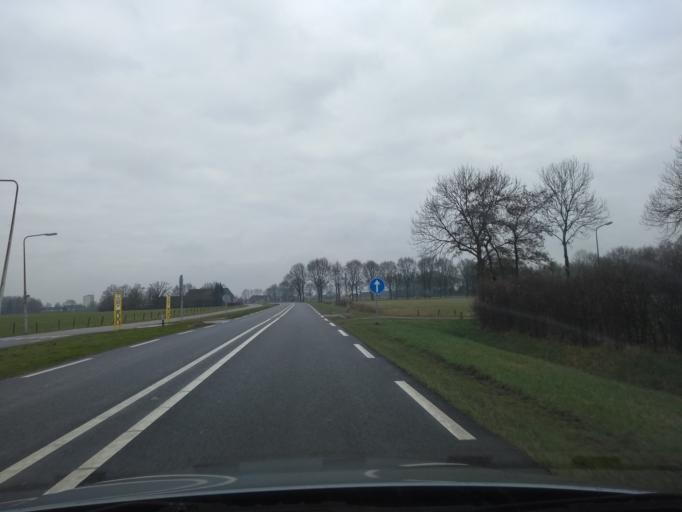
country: NL
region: Overijssel
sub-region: Gemeente Steenwijkerland
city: Vollenhove
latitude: 52.6741
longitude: 5.9726
